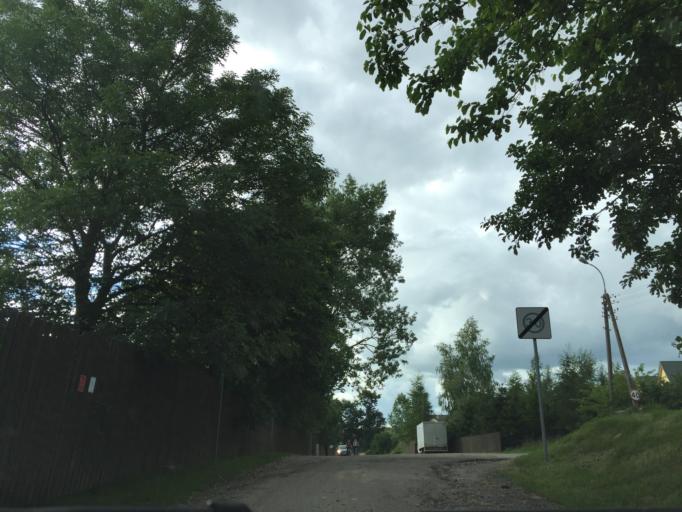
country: PL
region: Podlasie
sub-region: Suwalki
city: Suwalki
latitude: 54.1181
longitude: 22.9233
